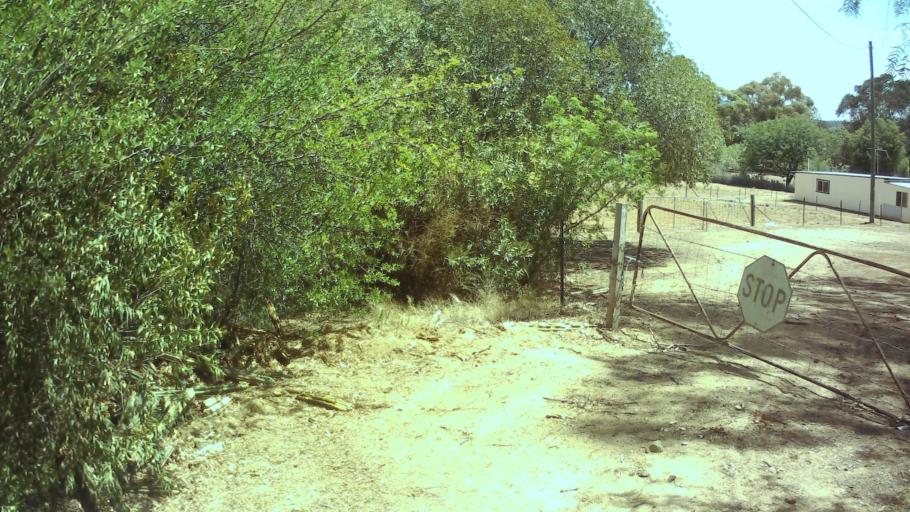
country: AU
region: New South Wales
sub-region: Weddin
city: Grenfell
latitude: -33.9032
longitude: 148.1661
